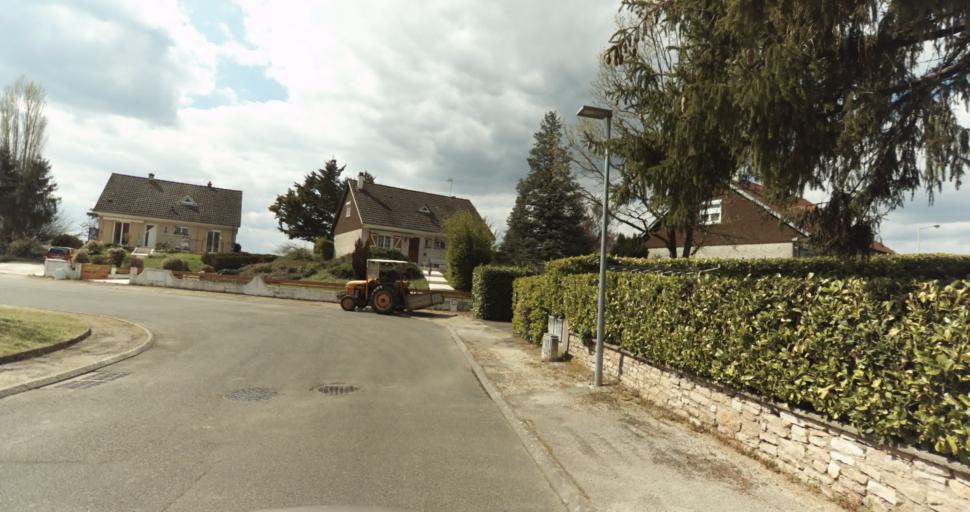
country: FR
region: Bourgogne
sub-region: Departement de la Cote-d'Or
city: Auxonne
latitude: 47.1962
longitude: 5.4127
